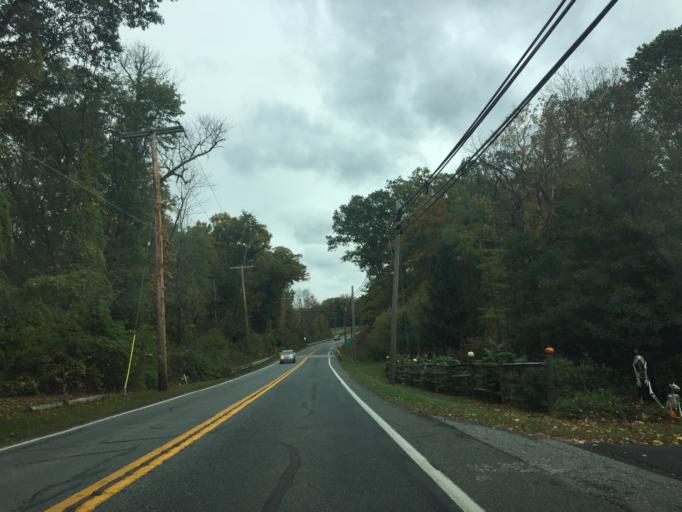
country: US
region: Maryland
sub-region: Harford County
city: Riverside
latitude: 39.5289
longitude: -76.2629
